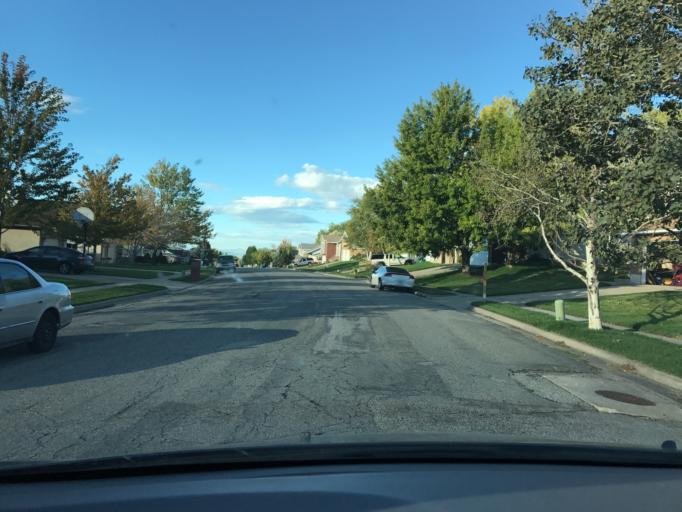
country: US
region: Utah
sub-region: Davis County
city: South Weber
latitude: 41.1085
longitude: -111.9224
